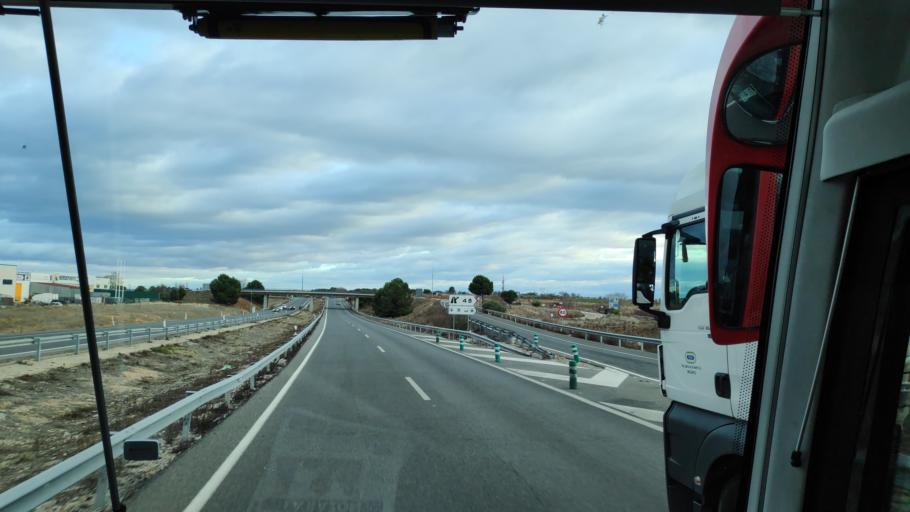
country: ES
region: Madrid
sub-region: Provincia de Madrid
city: Villarejo de Salvanes
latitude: 40.1734
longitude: -3.2944
